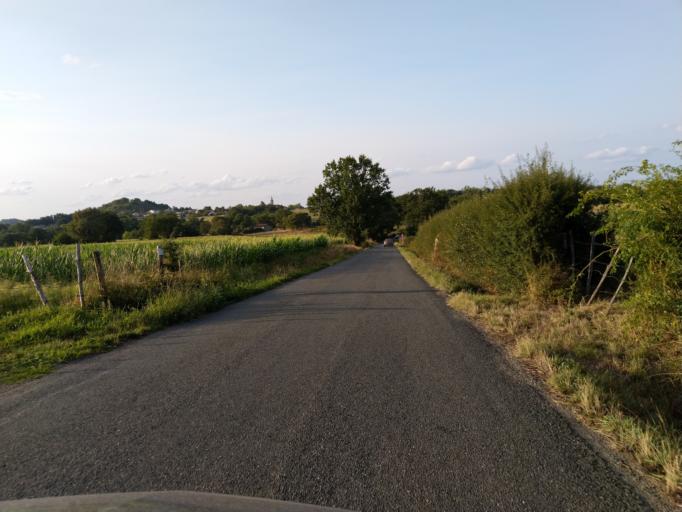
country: FR
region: Midi-Pyrenees
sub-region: Departement du Tarn
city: Frejairolles
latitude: 43.8706
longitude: 2.2336
